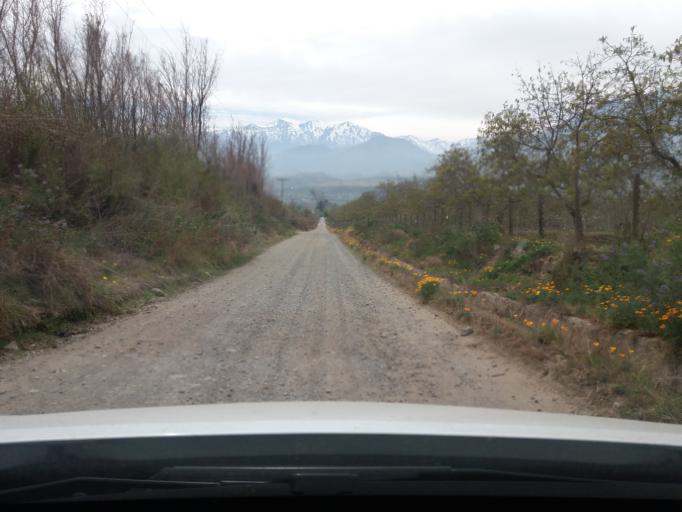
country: CL
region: Valparaiso
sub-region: Provincia de Los Andes
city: Los Andes
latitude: -32.8435
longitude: -70.5523
